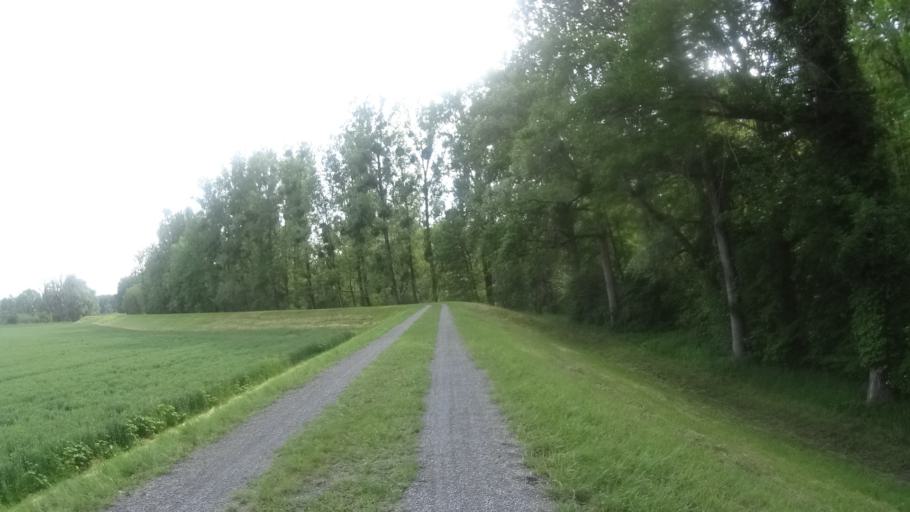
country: DE
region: Baden-Wuerttemberg
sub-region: Karlsruhe Region
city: Hugelsheim
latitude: 48.8145
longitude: 8.1173
